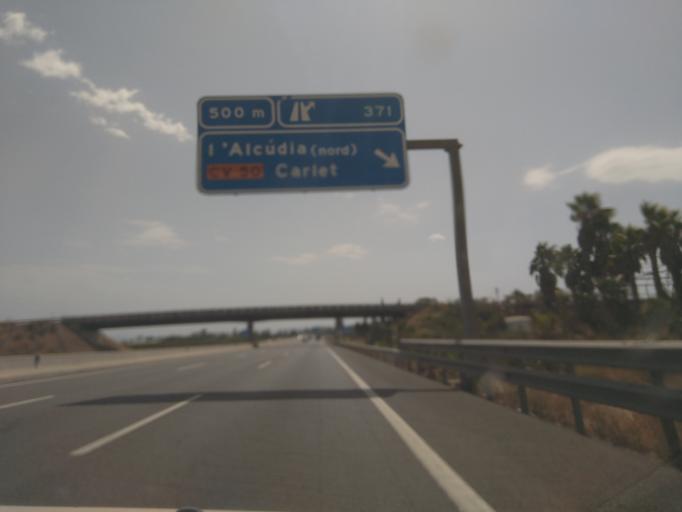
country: ES
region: Valencia
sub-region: Provincia de Valencia
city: L'Alcudia
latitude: 39.2176
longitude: -0.4943
